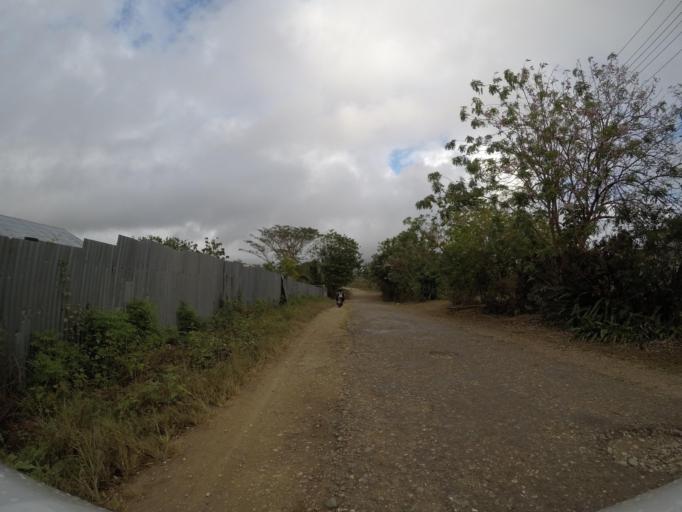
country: TL
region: Lautem
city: Lospalos
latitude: -8.5263
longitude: 126.9872
